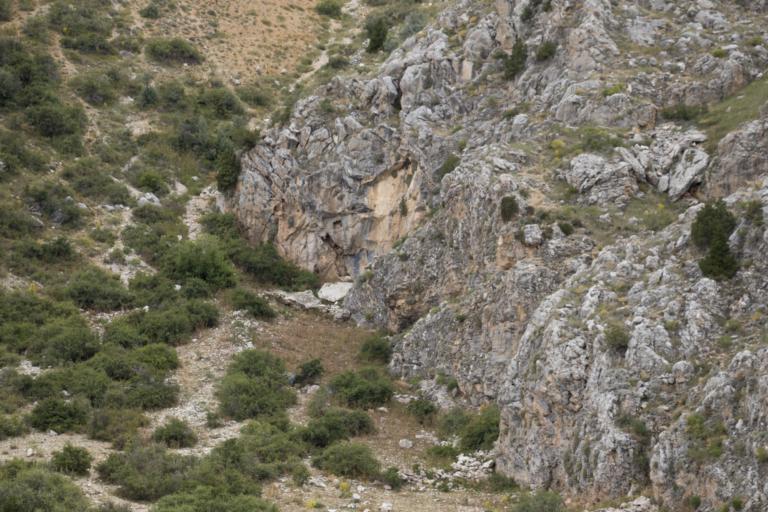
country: TR
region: Kayseri
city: Toklar
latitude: 38.4316
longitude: 36.1614
